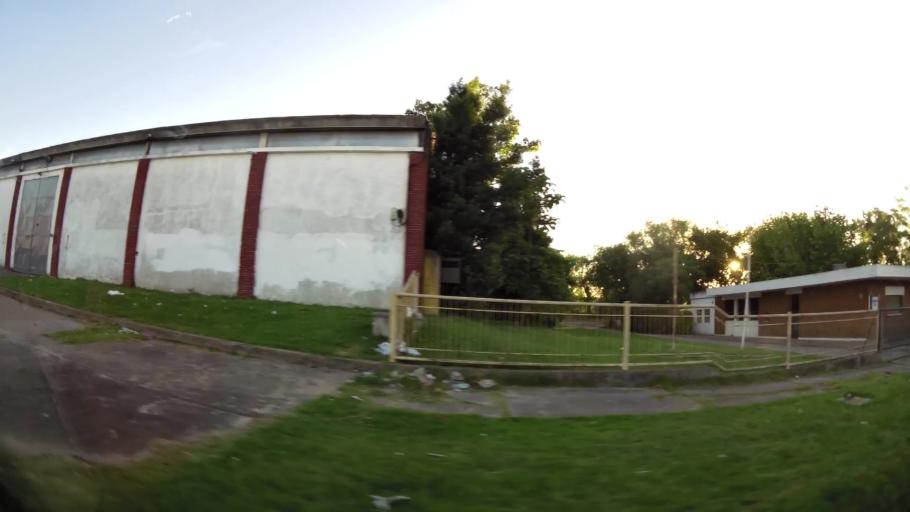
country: UY
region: Montevideo
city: Montevideo
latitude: -34.8461
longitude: -56.1588
